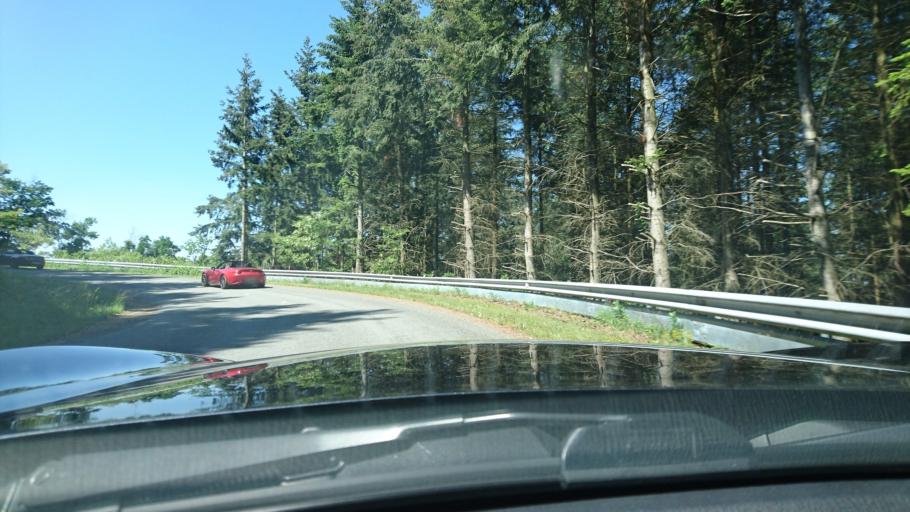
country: FR
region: Rhone-Alpes
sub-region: Departement de la Loire
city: Saint-Just-la-Pendue
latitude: 45.8616
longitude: 4.2444
